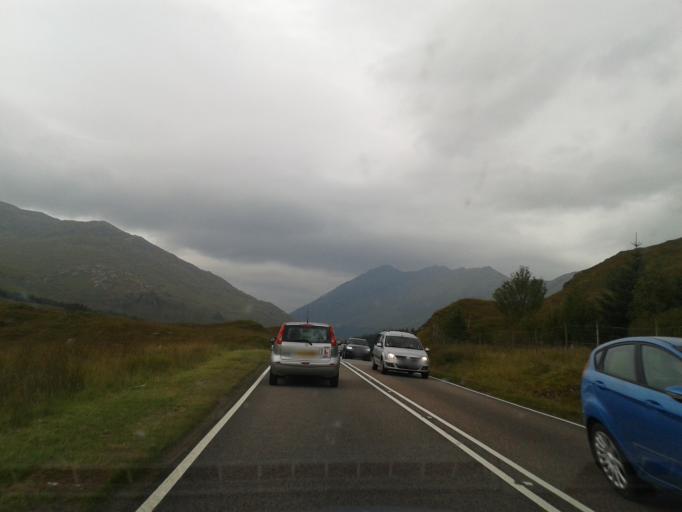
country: GB
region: Scotland
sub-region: Highland
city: Fort William
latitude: 57.1539
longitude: -5.2424
